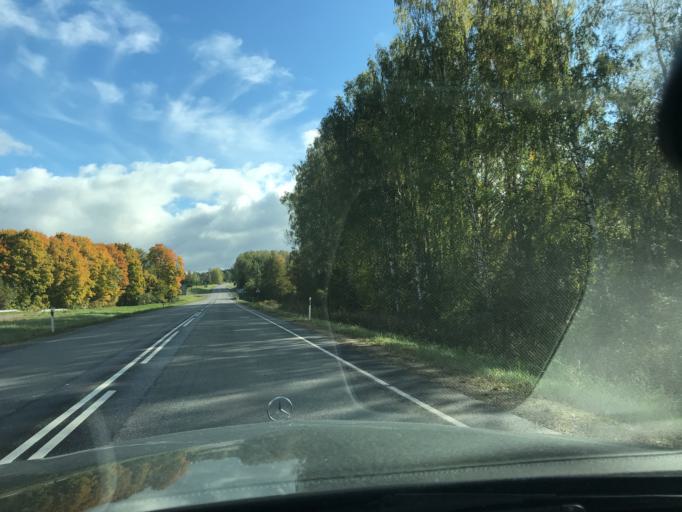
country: EE
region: Vorumaa
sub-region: Voru linn
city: Voru
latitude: 57.8085
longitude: 27.0683
